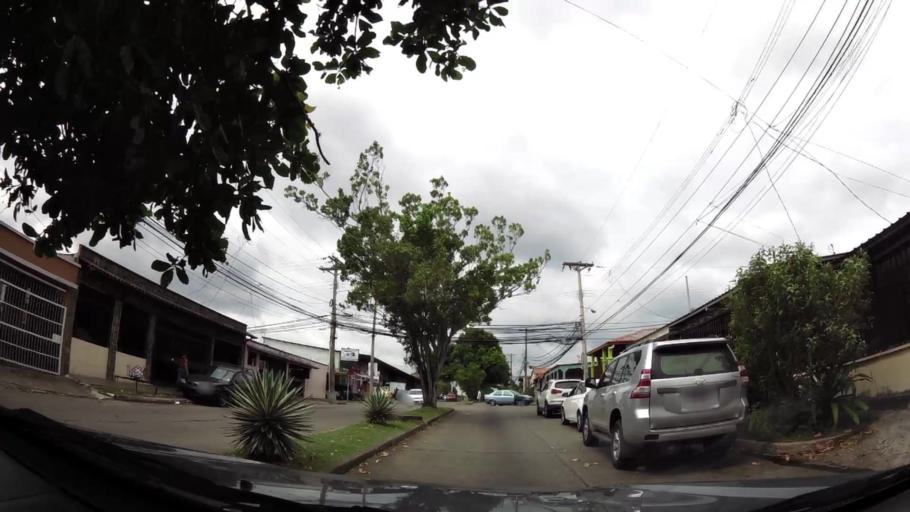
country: PA
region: Panama
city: San Miguelito
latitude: 9.0531
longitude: -79.4220
